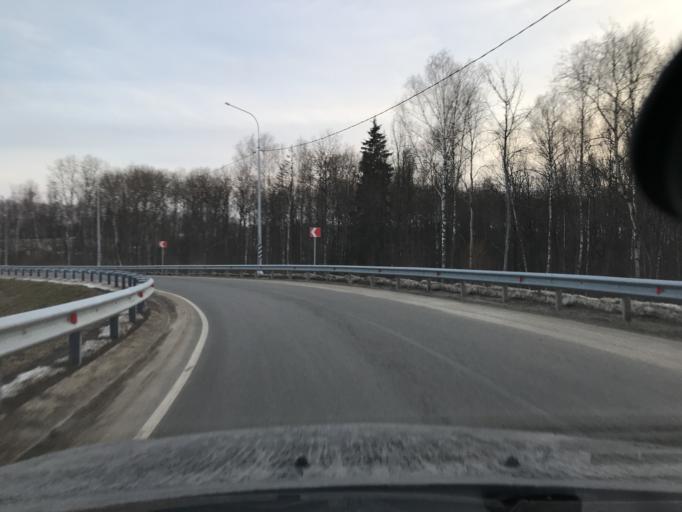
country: RU
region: Kaluga
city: Kaluga
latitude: 54.6389
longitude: 36.2990
